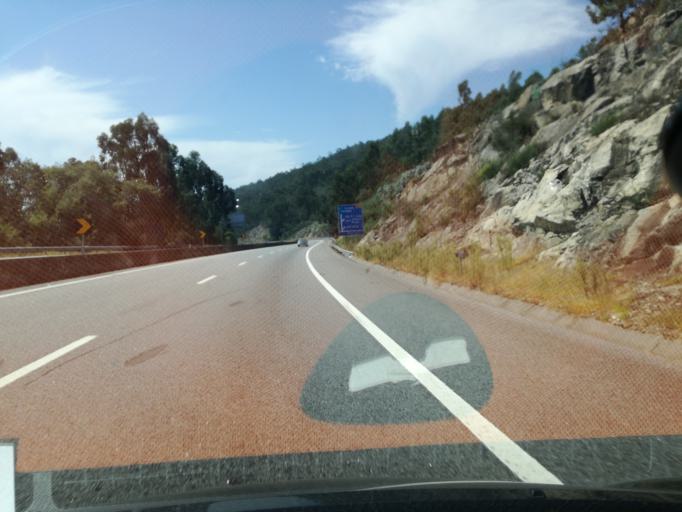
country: PT
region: Viana do Castelo
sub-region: Viana do Castelo
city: Meadela
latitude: 41.7268
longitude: -8.7956
